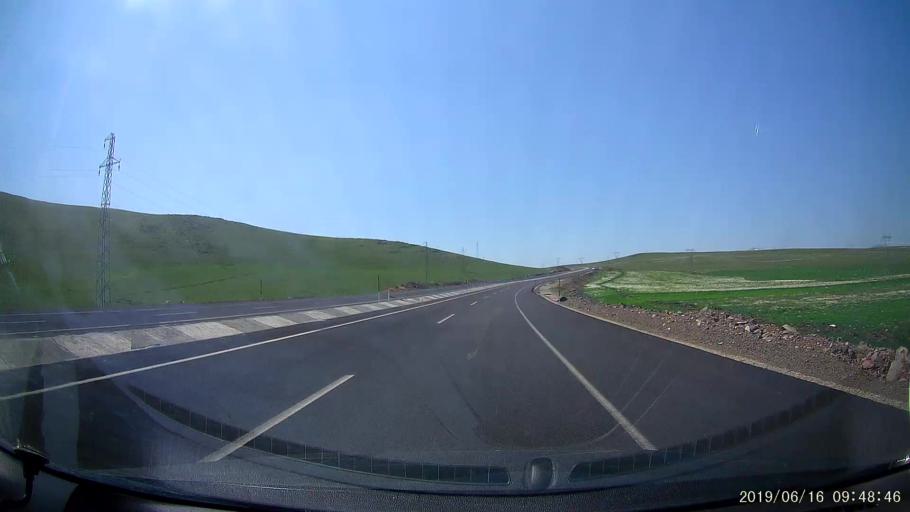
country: TR
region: Kars
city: Digor
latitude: 40.4299
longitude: 43.3554
